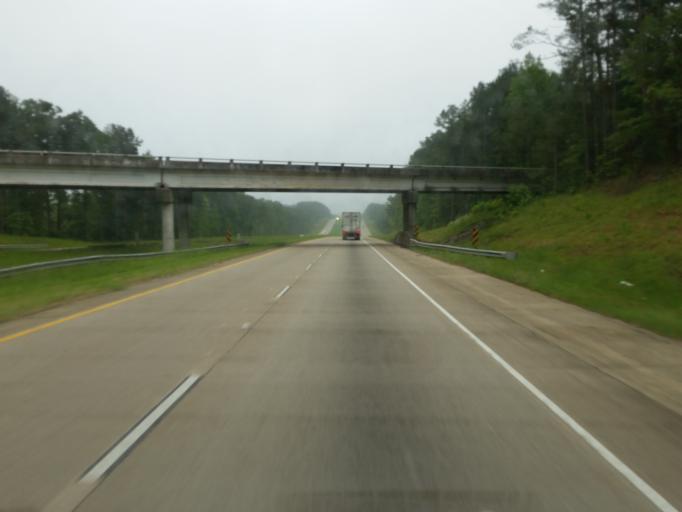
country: US
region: Louisiana
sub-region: Bienville Parish
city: Arcadia
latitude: 32.5615
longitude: -93.0140
